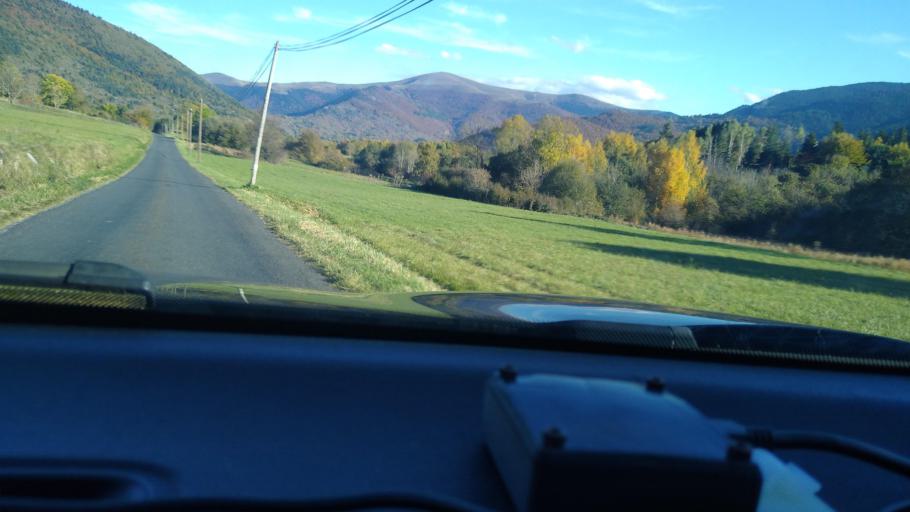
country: FR
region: Languedoc-Roussillon
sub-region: Departement de l'Aude
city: Quillan
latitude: 42.7460
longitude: 2.1815
